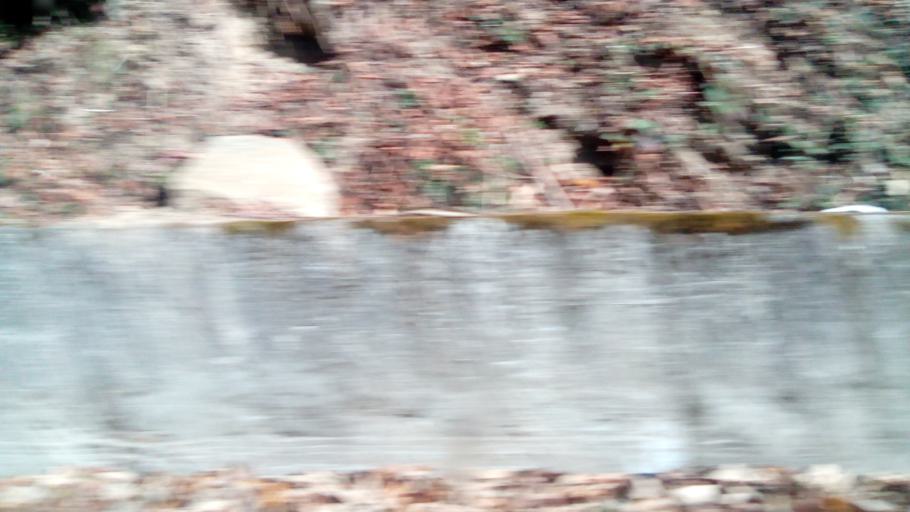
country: TW
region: Taiwan
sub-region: Hualien
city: Hualian
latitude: 24.3328
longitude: 121.3117
